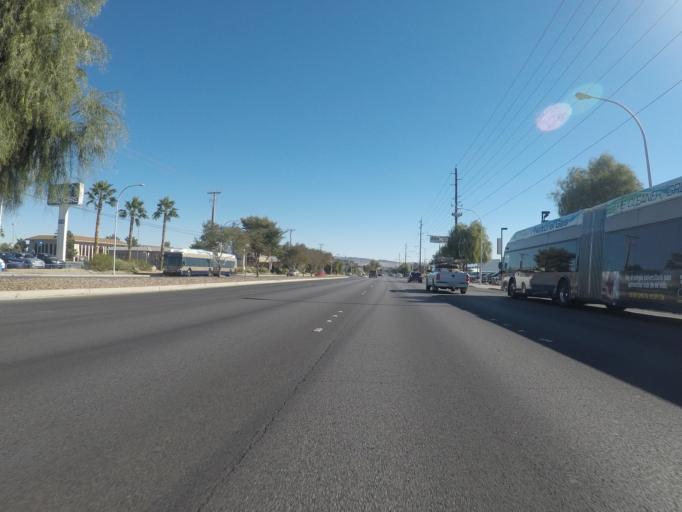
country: US
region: Nevada
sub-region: Clark County
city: Winchester
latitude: 36.1443
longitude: -115.1267
